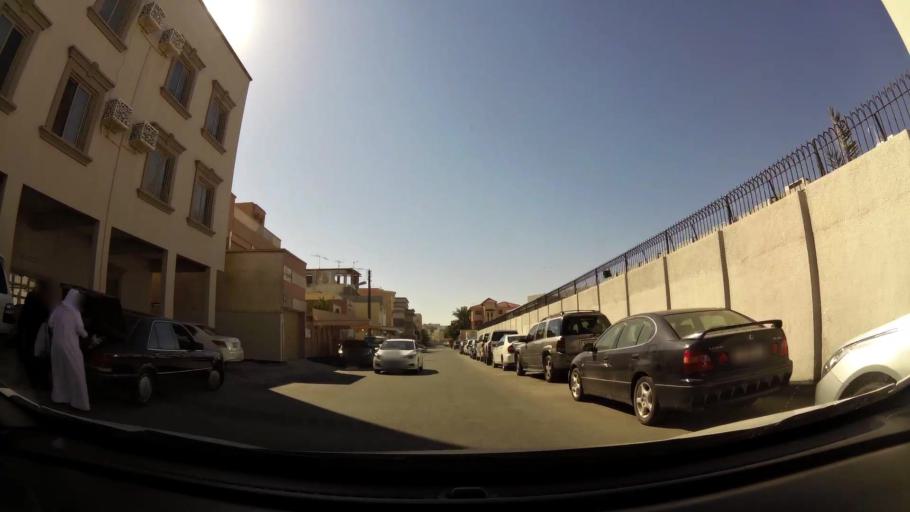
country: BH
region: Muharraq
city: Al Muharraq
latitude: 26.2626
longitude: 50.6200
